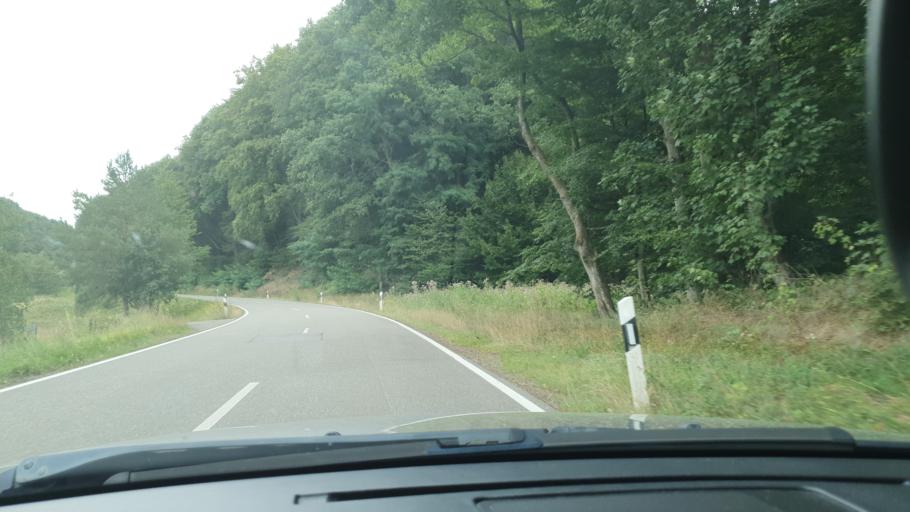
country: DE
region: Rheinland-Pfalz
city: Wallhalben
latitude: 49.3253
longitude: 7.5336
